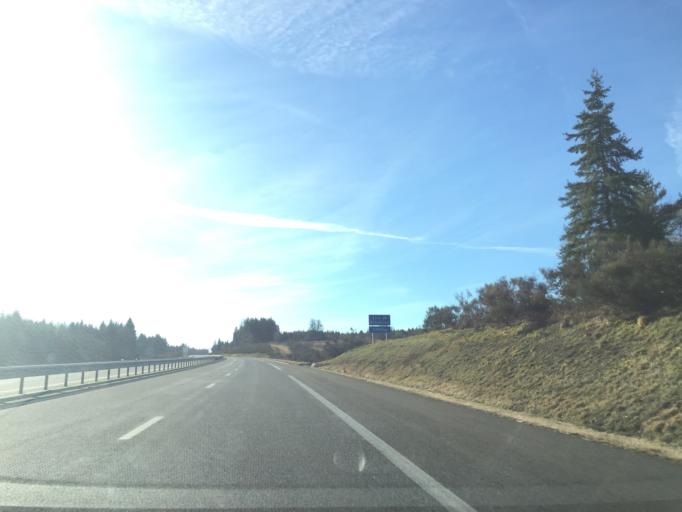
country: FR
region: Auvergne
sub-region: Departement du Puy-de-Dome
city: Gelles
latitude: 45.7469
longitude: 2.7144
